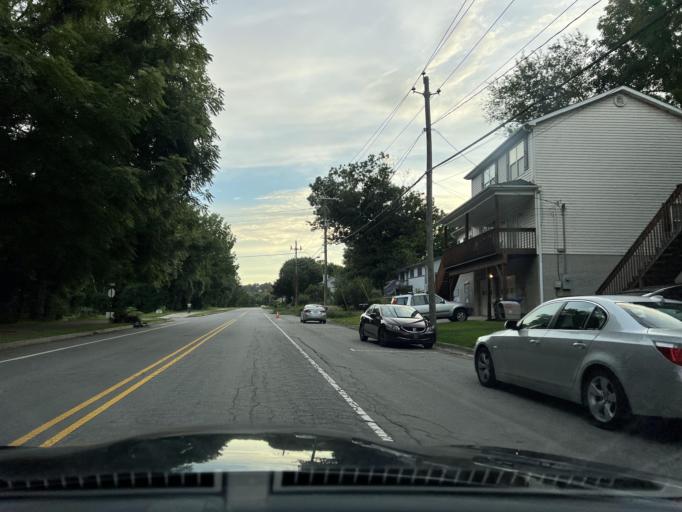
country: US
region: North Carolina
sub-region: Buncombe County
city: Asheville
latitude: 35.5815
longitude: -82.5567
